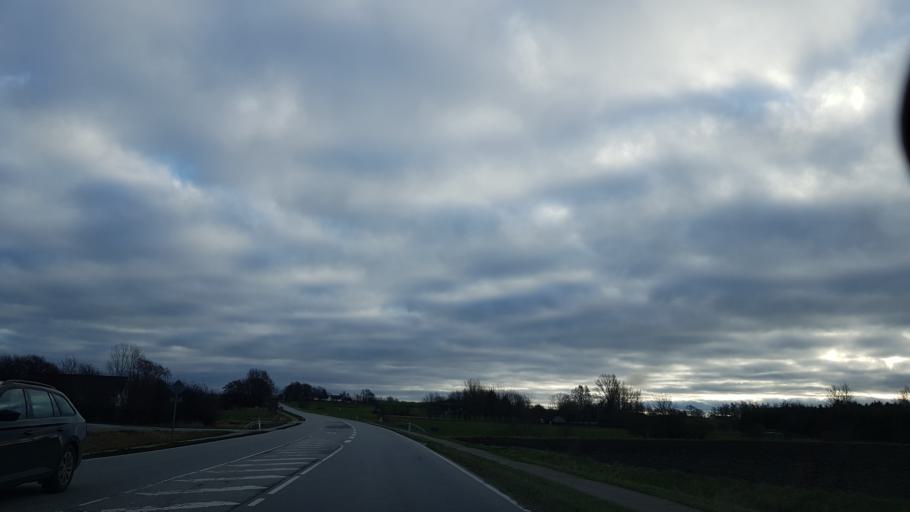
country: DK
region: Zealand
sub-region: Kalundborg Kommune
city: Hong
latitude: 55.5030
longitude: 11.2663
